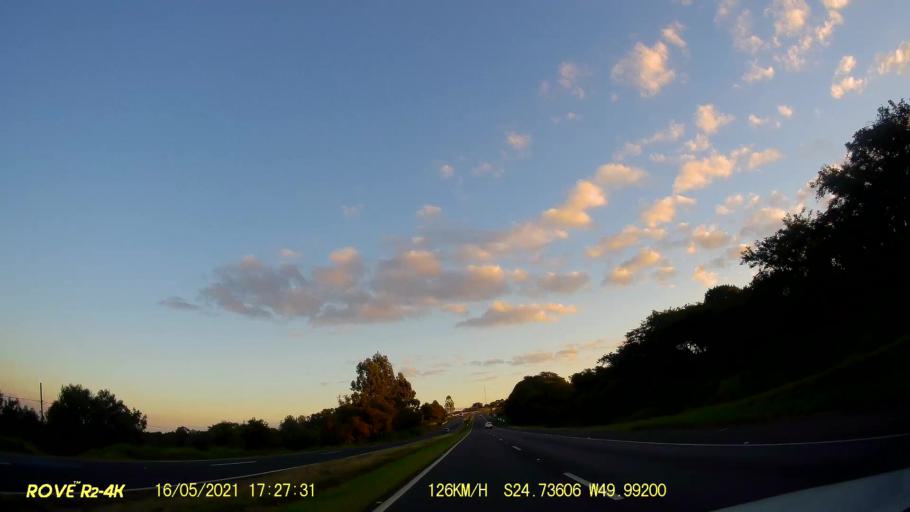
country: BR
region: Parana
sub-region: Castro
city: Castro
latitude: -24.7365
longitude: -49.9922
